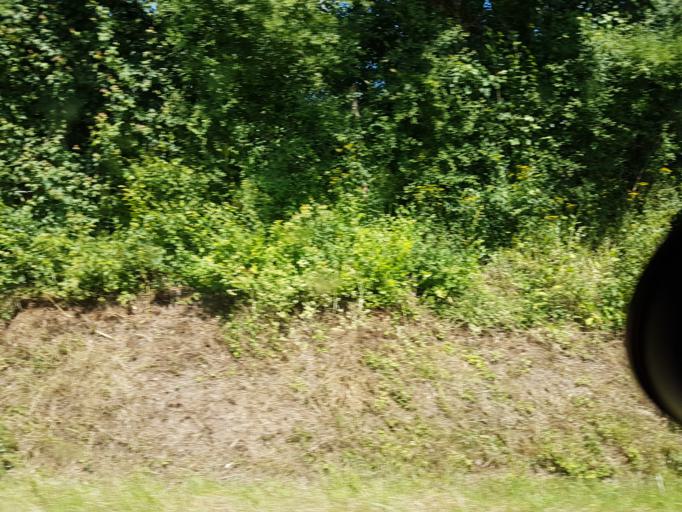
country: FR
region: Bourgogne
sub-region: Departement de Saone-et-Loire
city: Autun
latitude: 47.0515
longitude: 4.3008
